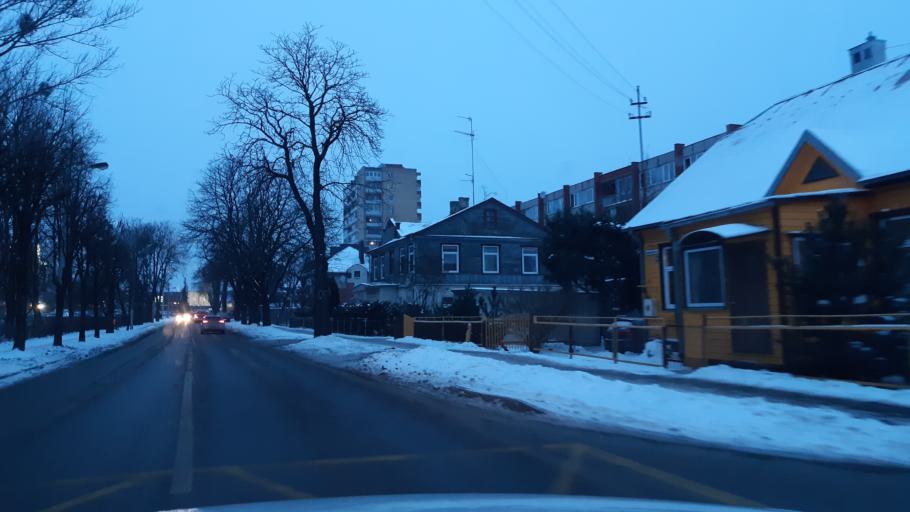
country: LT
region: Kauno apskritis
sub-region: Kaunas
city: Eiguliai
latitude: 54.9120
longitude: 23.9422
